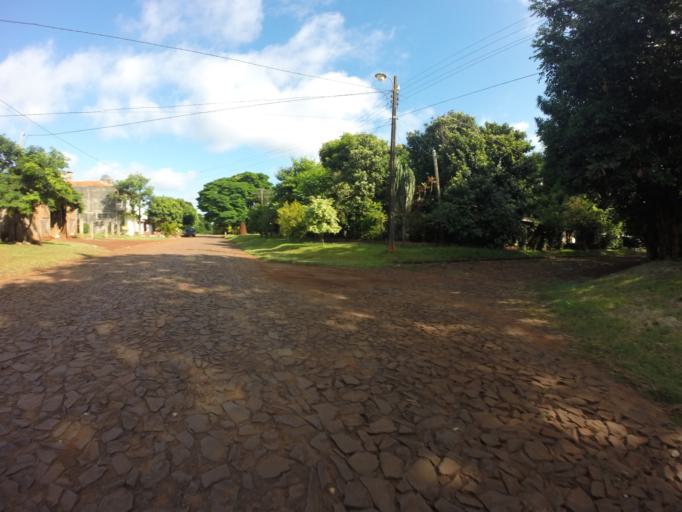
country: PY
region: Alto Parana
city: Ciudad del Este
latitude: -25.4025
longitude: -54.6466
